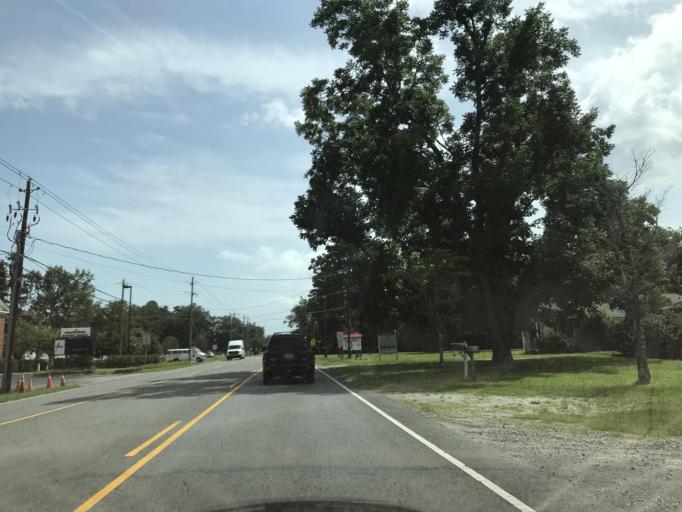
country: US
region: North Carolina
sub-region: New Hanover County
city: Wrightsboro
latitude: 34.2939
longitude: -77.9213
